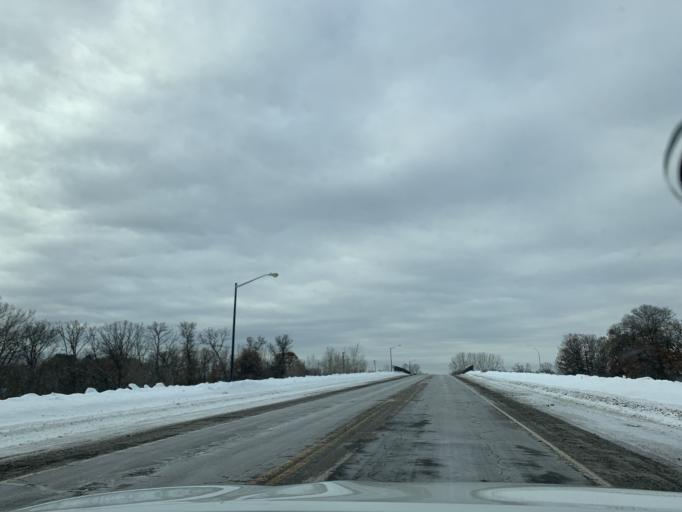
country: US
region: Minnesota
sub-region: Hennepin County
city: West Coon Rapids
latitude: 45.1766
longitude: -93.3008
